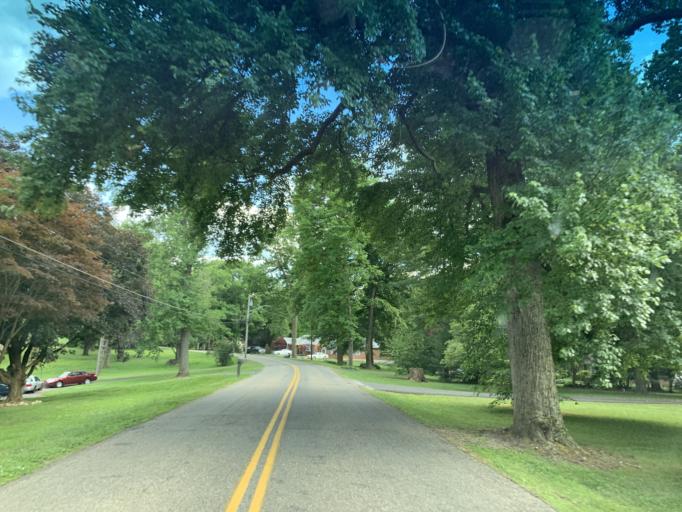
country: US
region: Maryland
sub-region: Harford County
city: Jarrettsville
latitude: 39.5599
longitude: -76.4495
